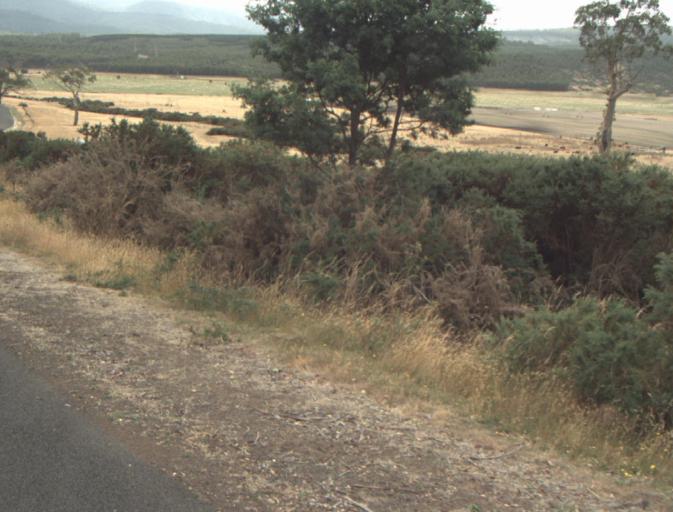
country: AU
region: Tasmania
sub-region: Northern Midlands
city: Evandale
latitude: -41.5109
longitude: 147.4779
